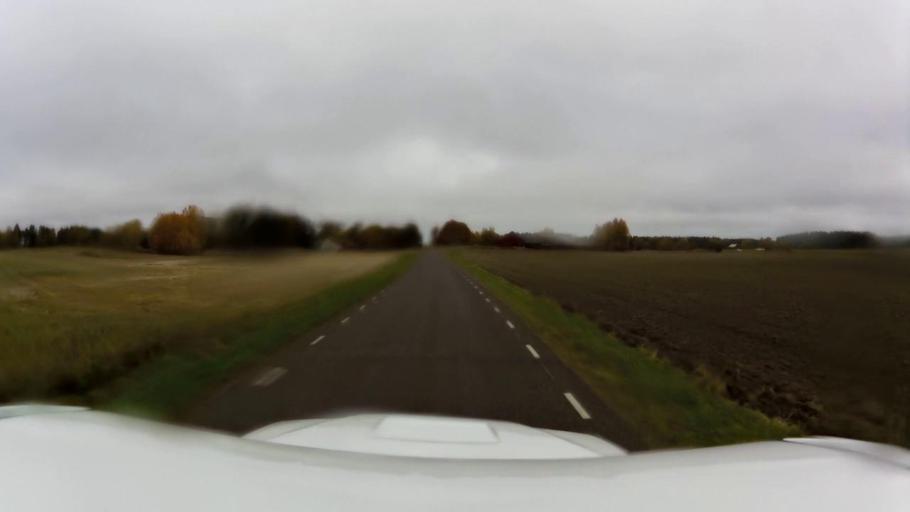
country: SE
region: OEstergoetland
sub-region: Linkopings Kommun
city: Linghem
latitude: 58.4608
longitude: 15.7747
